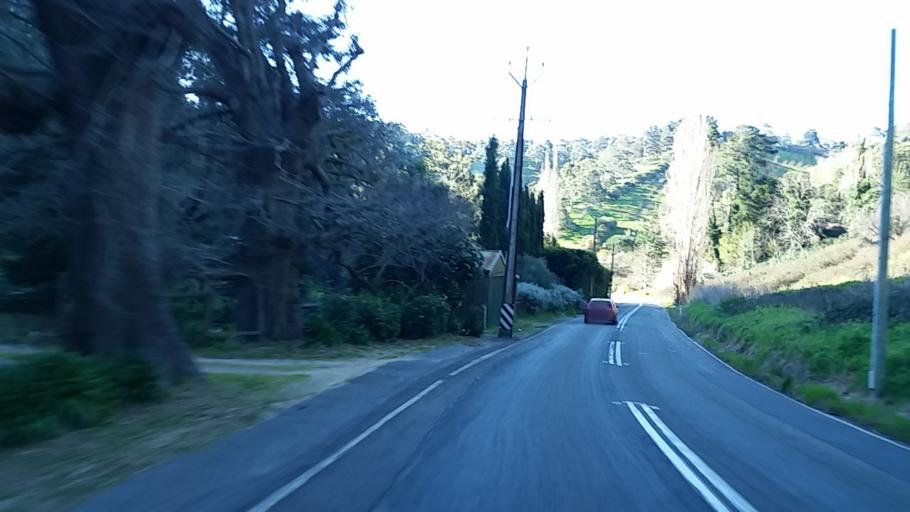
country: AU
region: South Australia
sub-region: Adelaide Hills
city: Adelaide Hills
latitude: -34.9248
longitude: 138.7180
